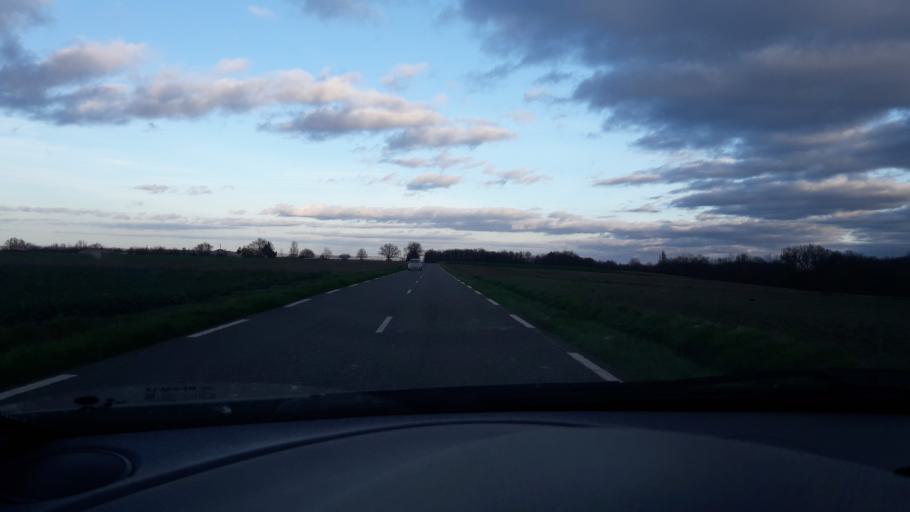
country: FR
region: Midi-Pyrenees
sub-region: Departement de la Haute-Garonne
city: Launac
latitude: 43.7451
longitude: 1.1502
